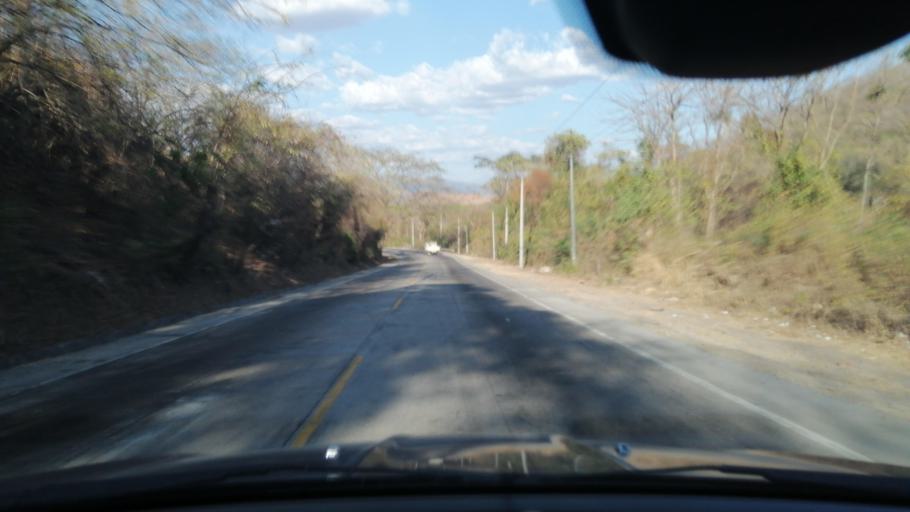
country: SV
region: Santa Ana
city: Texistepeque
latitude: 14.0644
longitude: -89.5058
